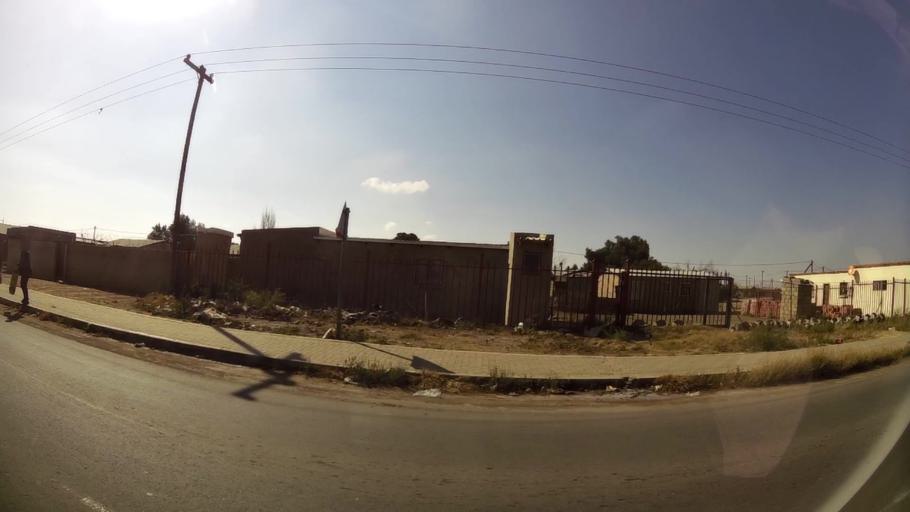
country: ZA
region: Orange Free State
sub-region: Mangaung Metropolitan Municipality
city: Bloemfontein
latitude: -29.1603
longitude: 26.2782
